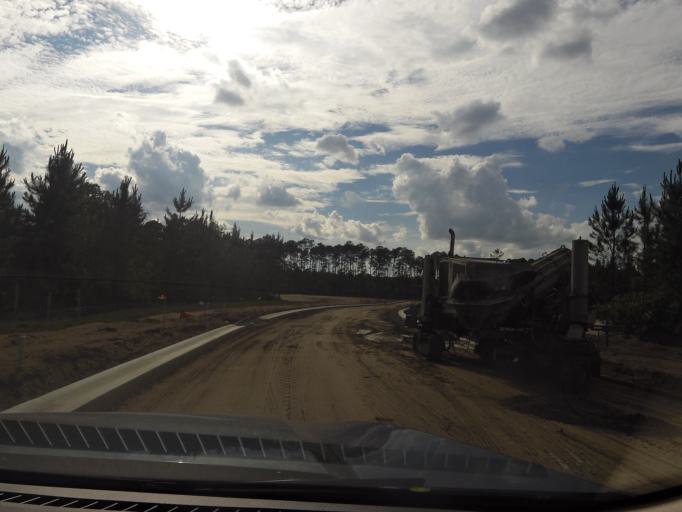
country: US
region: Florida
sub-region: Saint Johns County
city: Palm Valley
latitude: 30.1824
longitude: -81.5103
